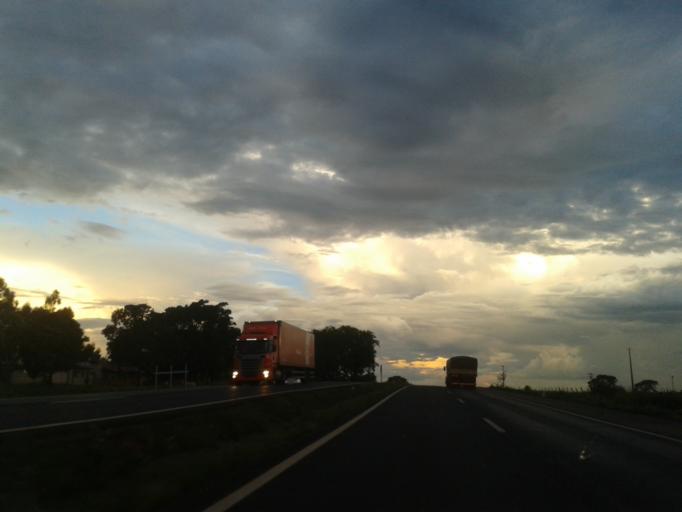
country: BR
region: Minas Gerais
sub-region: Centralina
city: Centralina
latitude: -18.7263
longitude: -49.1163
